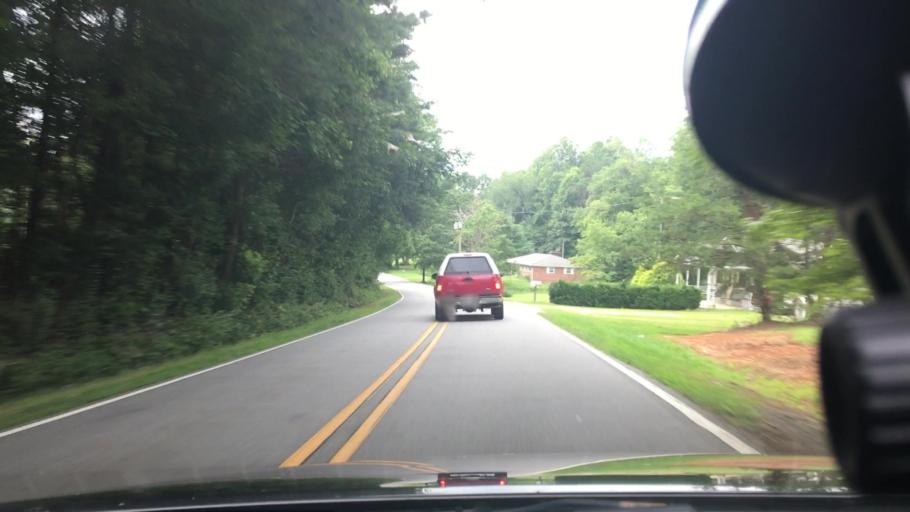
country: US
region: North Carolina
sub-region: McDowell County
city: West Marion
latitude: 35.6455
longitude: -82.0156
